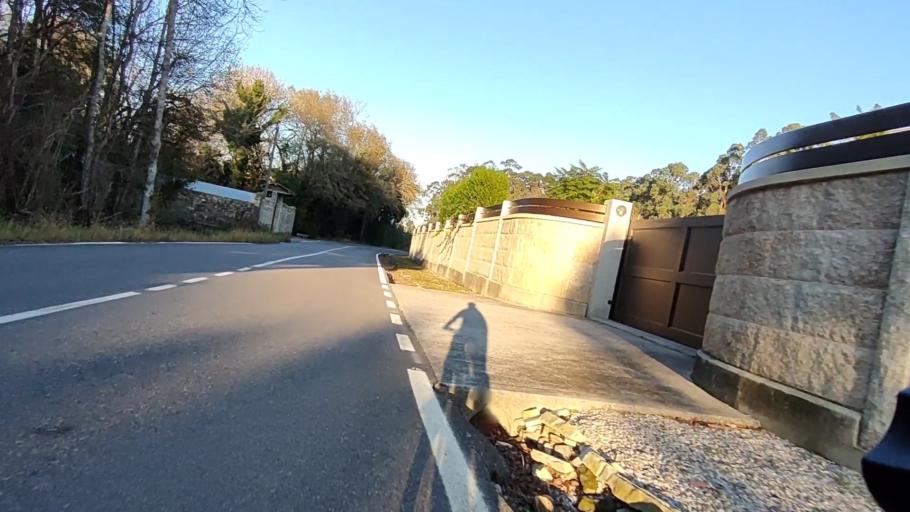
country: ES
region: Galicia
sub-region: Provincia da Coruna
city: Boiro
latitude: 42.6323
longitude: -8.8600
